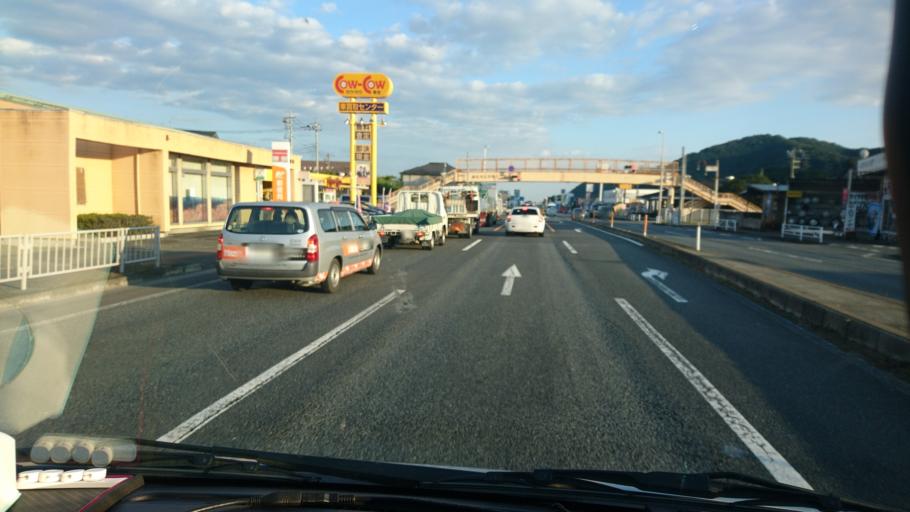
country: JP
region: Gunma
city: Kiryu
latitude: 36.3771
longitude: 139.3464
